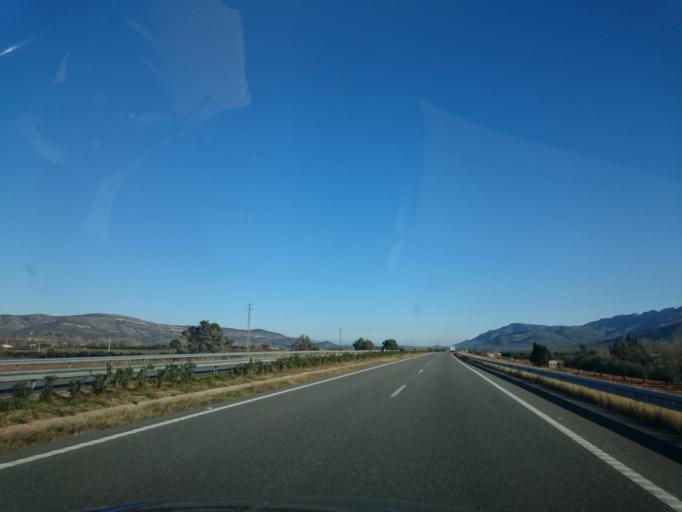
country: ES
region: Catalonia
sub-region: Provincia de Tarragona
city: Ulldecona
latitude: 40.5837
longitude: 0.4567
